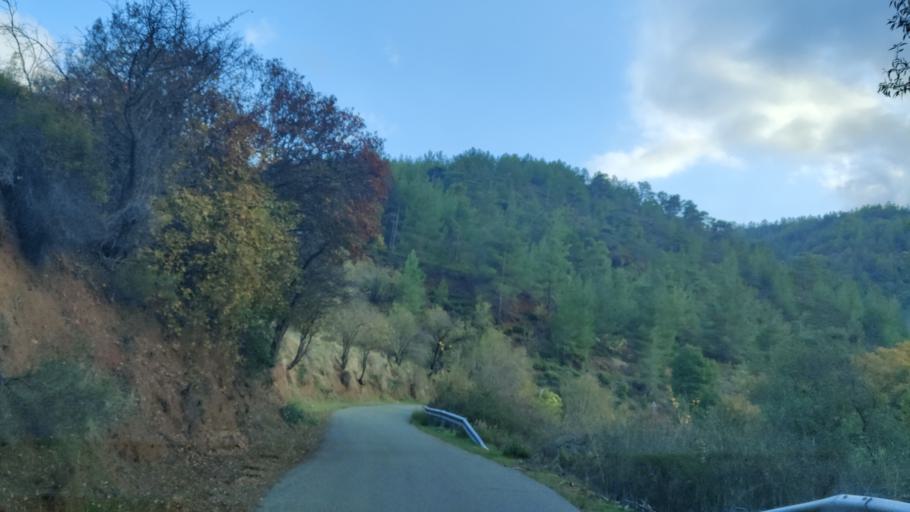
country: CY
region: Lefkosia
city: Lefka
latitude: 35.0724
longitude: 32.7421
